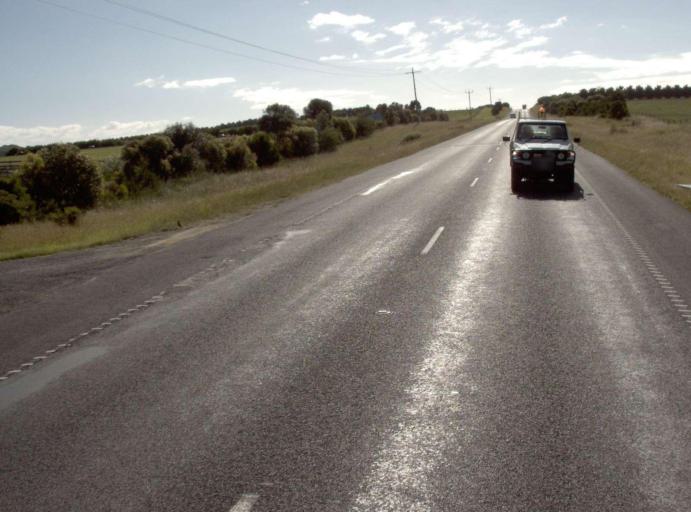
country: AU
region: Victoria
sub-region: Bass Coast
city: North Wonthaggi
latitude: -38.5611
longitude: 145.5108
